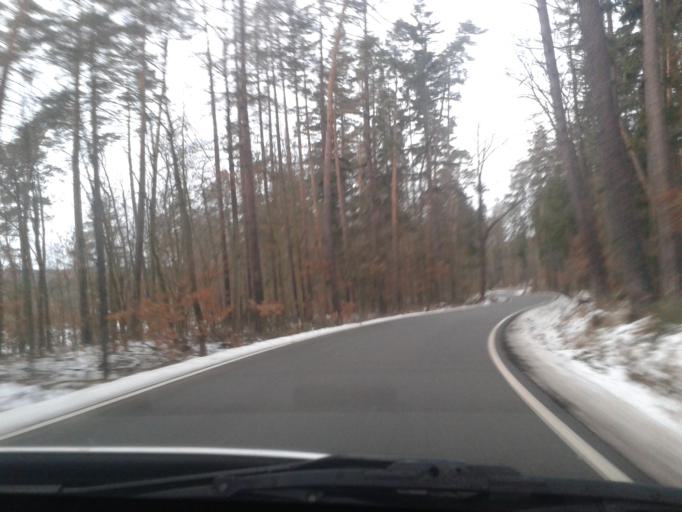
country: CZ
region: Olomoucky
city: Pteni
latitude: 49.5073
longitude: 16.9294
